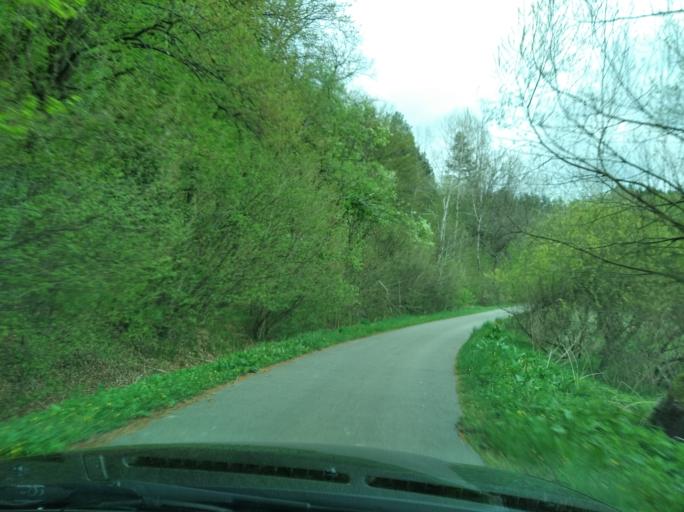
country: PL
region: Subcarpathian Voivodeship
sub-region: Powiat brzozowski
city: Dydnia
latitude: 49.6570
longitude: 22.2648
